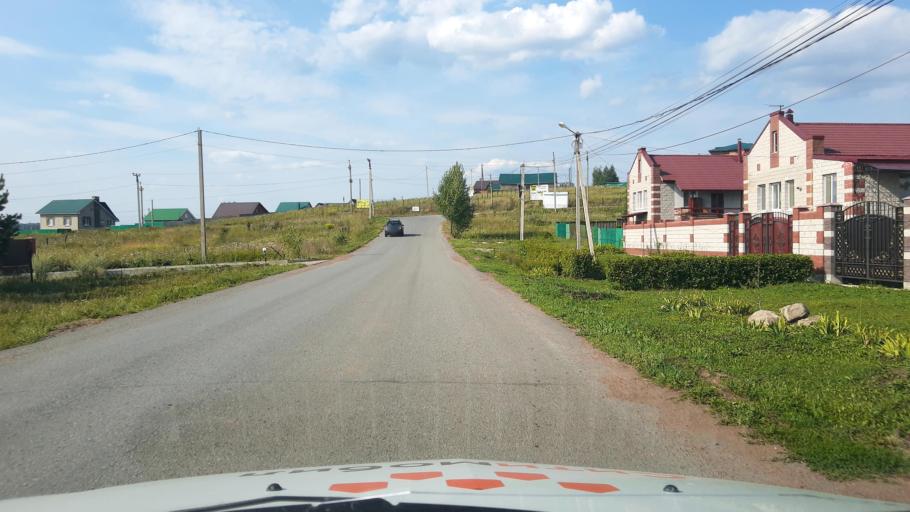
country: RU
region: Bashkortostan
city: Kabakovo
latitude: 54.6657
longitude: 56.2139
